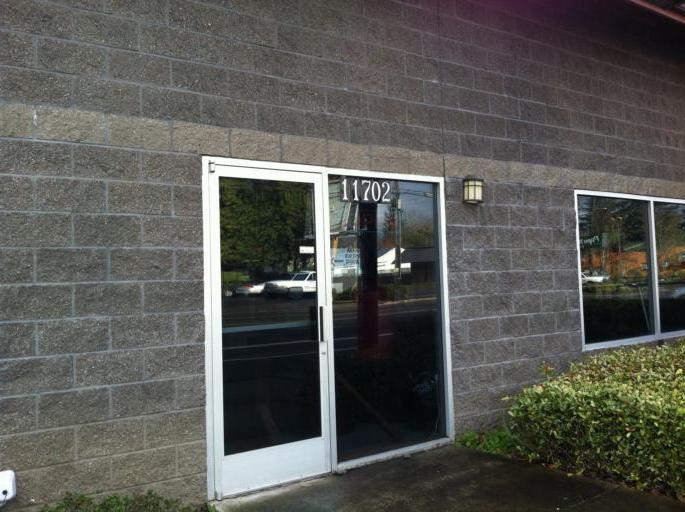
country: US
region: Oregon
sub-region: Multnomah County
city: Lents
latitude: 45.5334
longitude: -122.5424
